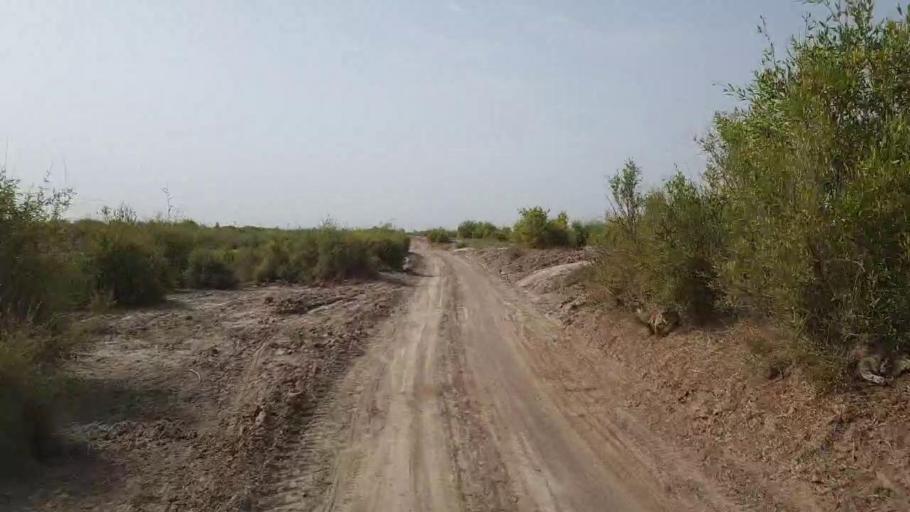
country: PK
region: Sindh
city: Daur
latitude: 26.4271
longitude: 68.1584
